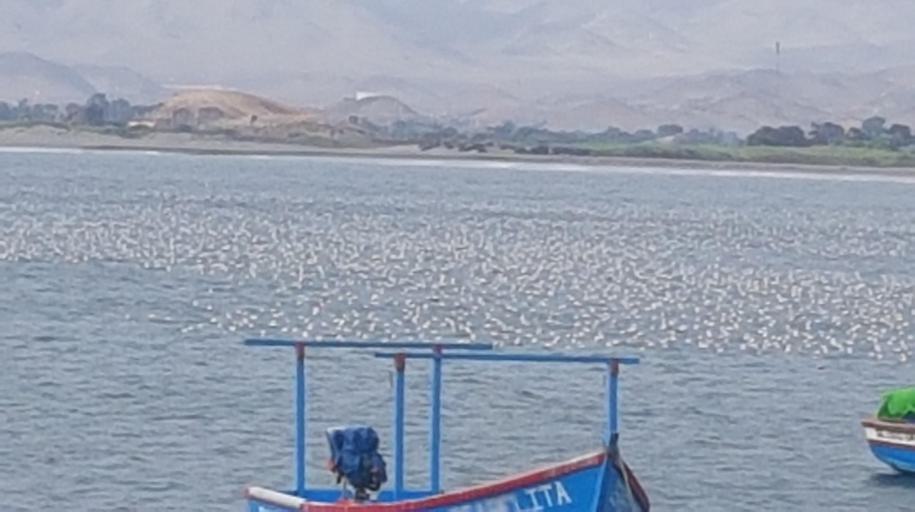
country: PE
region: Ancash
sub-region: Provincia de Huarmey
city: Huarmey
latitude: -10.0969
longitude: -78.1711
